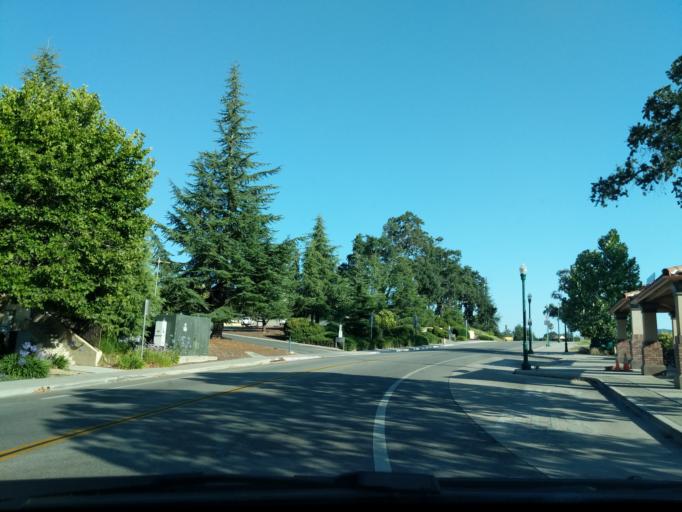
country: US
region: California
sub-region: San Luis Obispo County
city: Atascadero
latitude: 35.4892
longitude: -120.6648
